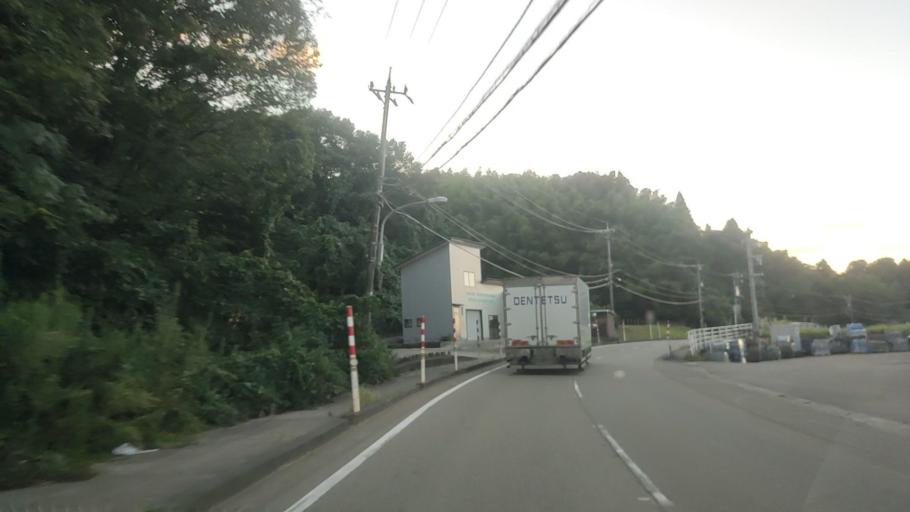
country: JP
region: Ishikawa
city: Tsubata
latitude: 36.6565
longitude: 136.7566
